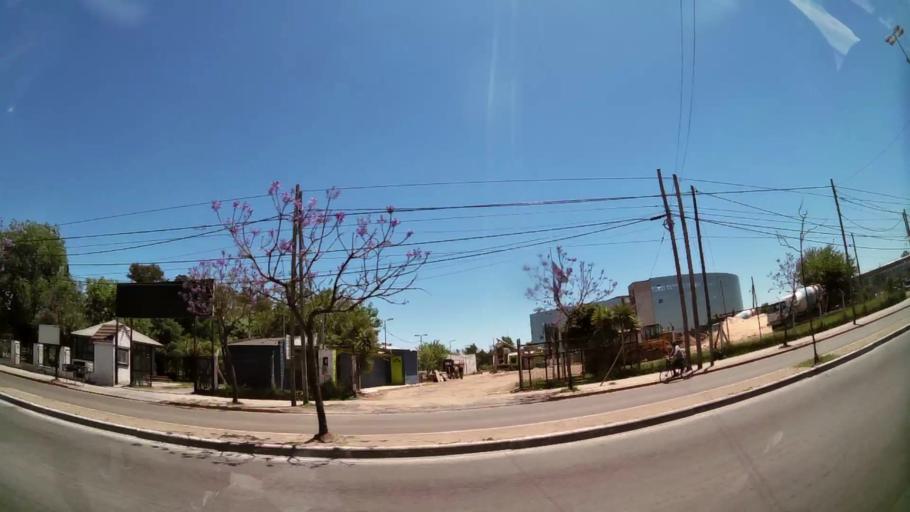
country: AR
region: Buenos Aires
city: Santa Catalina - Dique Lujan
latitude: -34.4979
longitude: -58.7089
